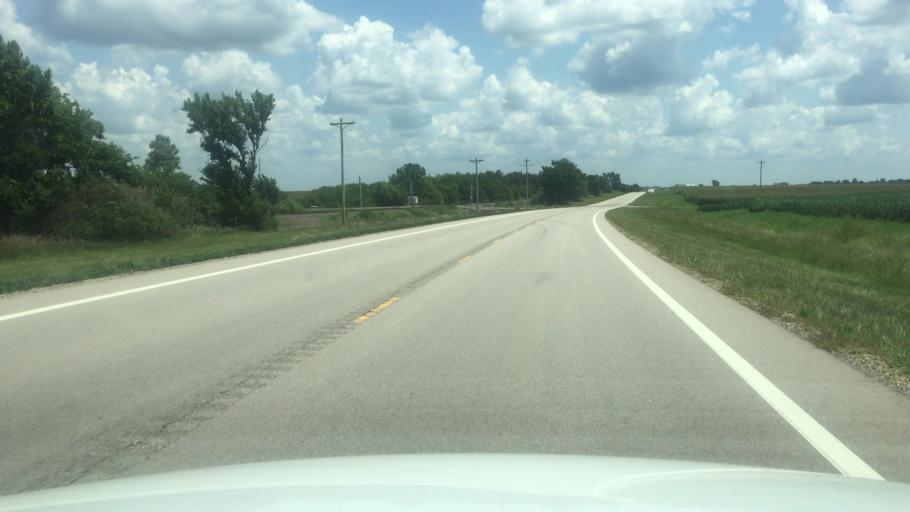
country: US
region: Kansas
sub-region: Brown County
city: Horton
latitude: 39.6591
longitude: -95.3796
